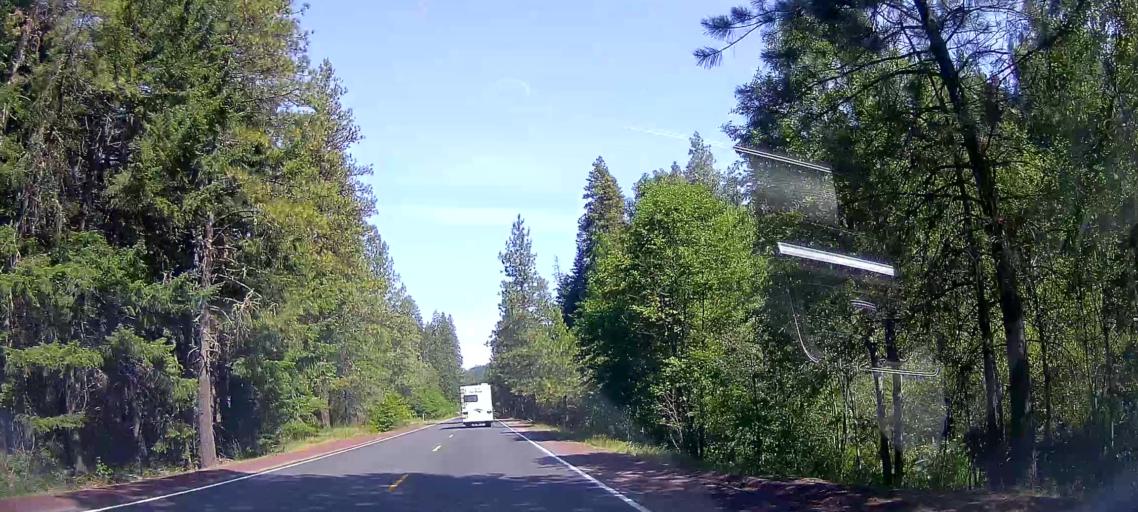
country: US
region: Oregon
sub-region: Jefferson County
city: Warm Springs
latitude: 45.0646
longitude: -121.5219
